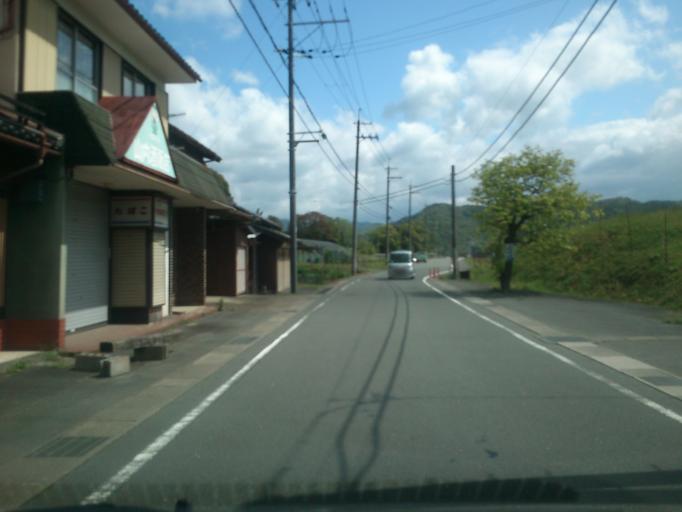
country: JP
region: Kyoto
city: Ayabe
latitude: 35.1810
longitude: 135.4084
